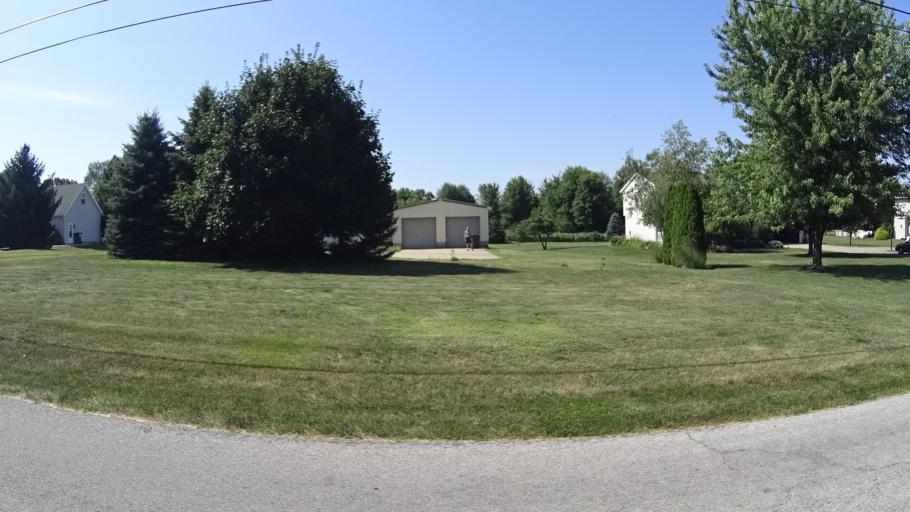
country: US
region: Ohio
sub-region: Huron County
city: Bellevue
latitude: 41.3722
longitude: -82.8434
